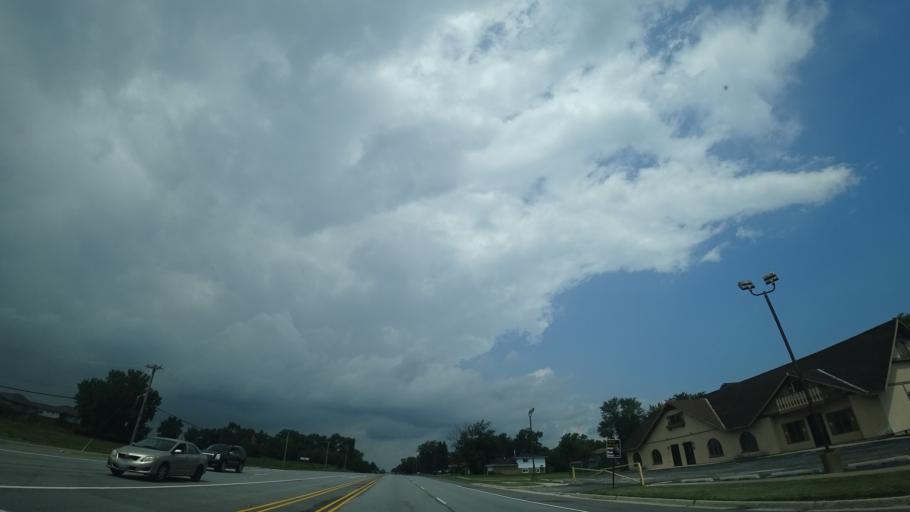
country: US
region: Illinois
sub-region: Cook County
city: Country Club Hills
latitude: 41.5428
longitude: -87.7327
